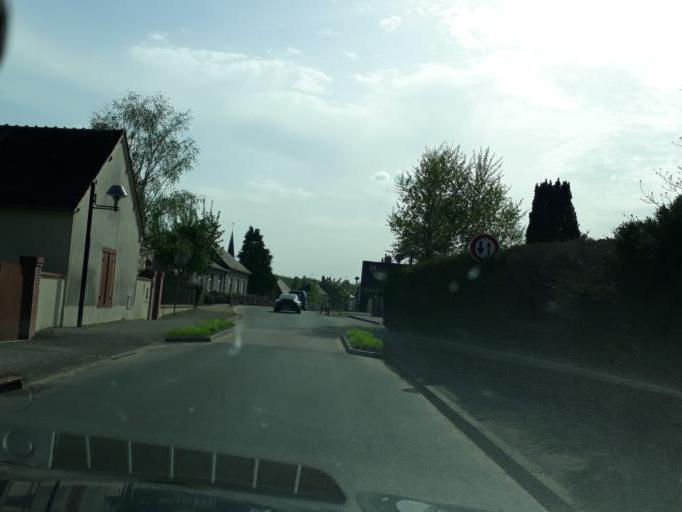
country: FR
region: Centre
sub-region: Departement du Loir-et-Cher
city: Saint-Laurent-Nouan
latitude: 47.6518
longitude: 1.6110
